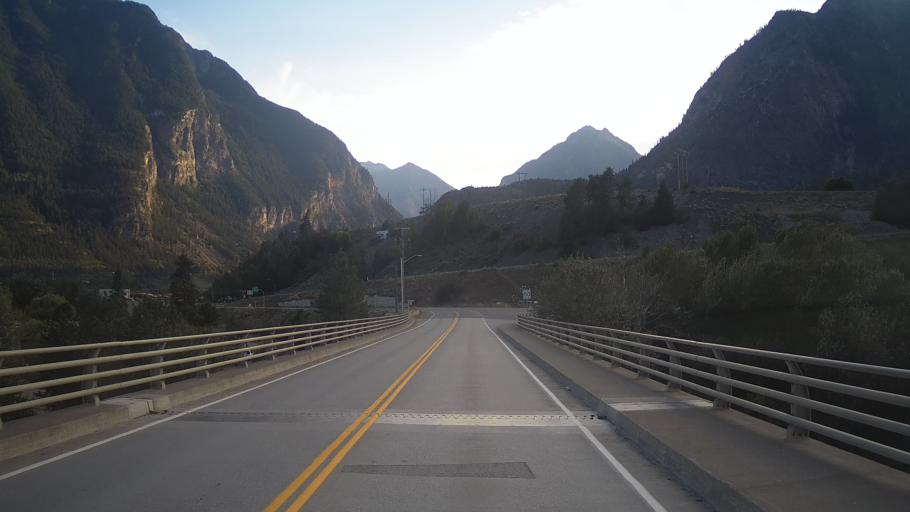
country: CA
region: British Columbia
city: Lillooet
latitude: 50.6835
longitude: -121.9293
